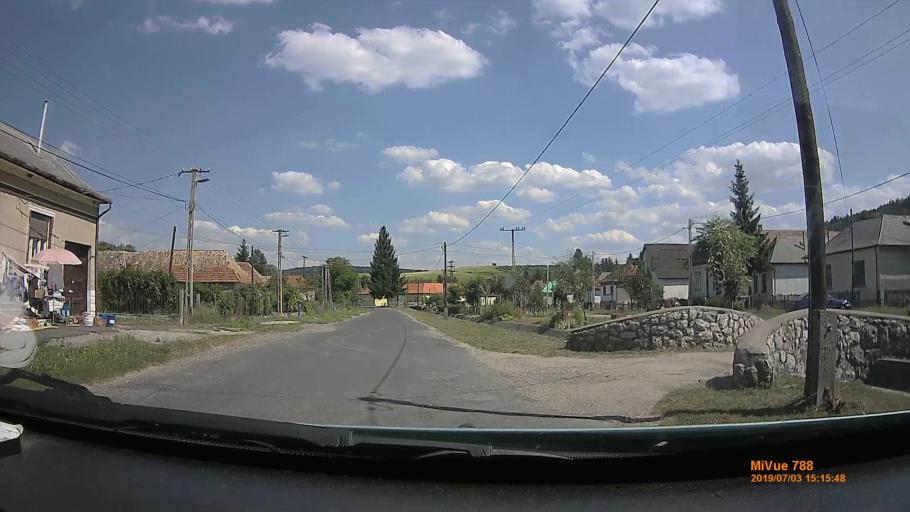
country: HU
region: Borsod-Abauj-Zemplen
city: Farkaslyuk
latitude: 48.2128
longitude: 20.3948
